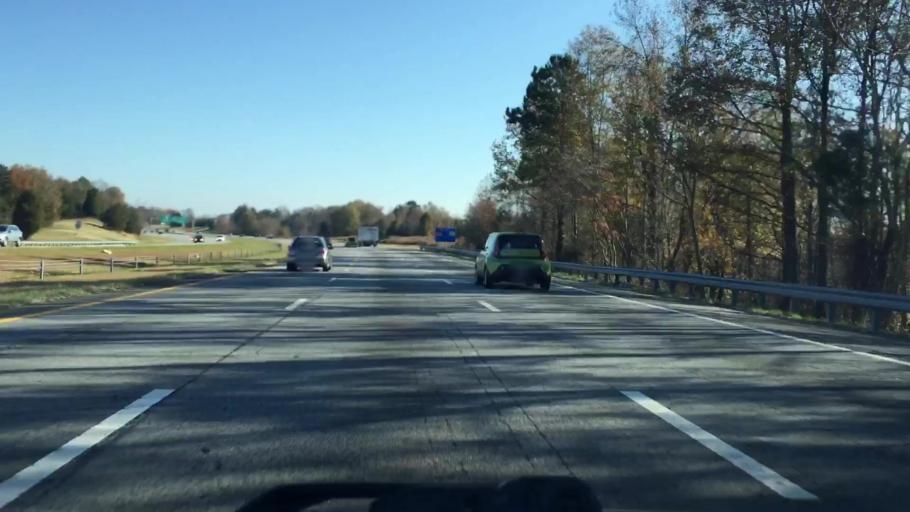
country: US
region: North Carolina
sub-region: Randolph County
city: Archdale
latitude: 35.8983
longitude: -79.9617
